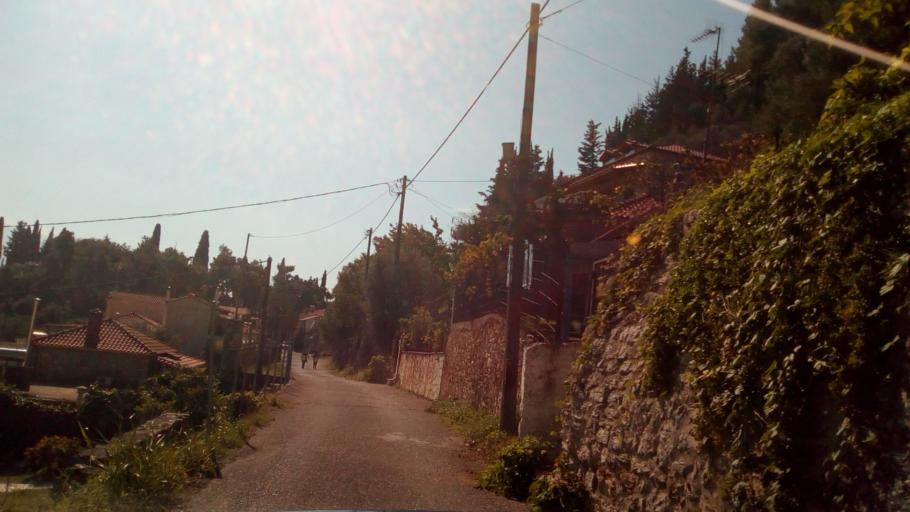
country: GR
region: West Greece
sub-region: Nomos Aitolias kai Akarnanias
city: Nafpaktos
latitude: 38.3975
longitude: 21.8408
